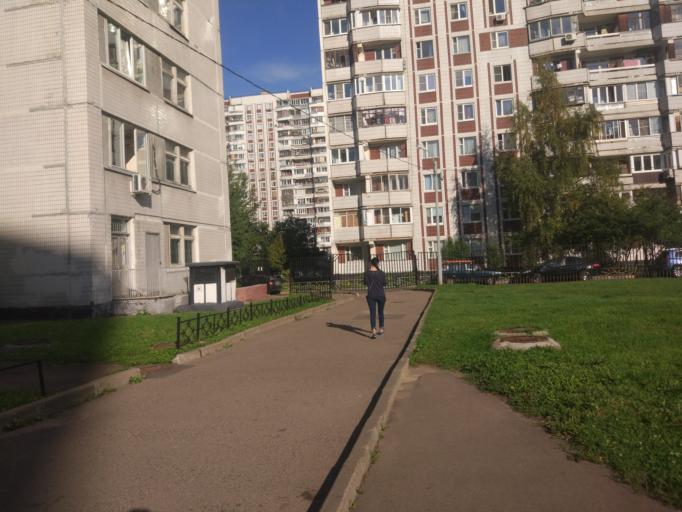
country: RU
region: Moskovskaya
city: Reutov
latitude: 55.7426
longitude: 37.8756
